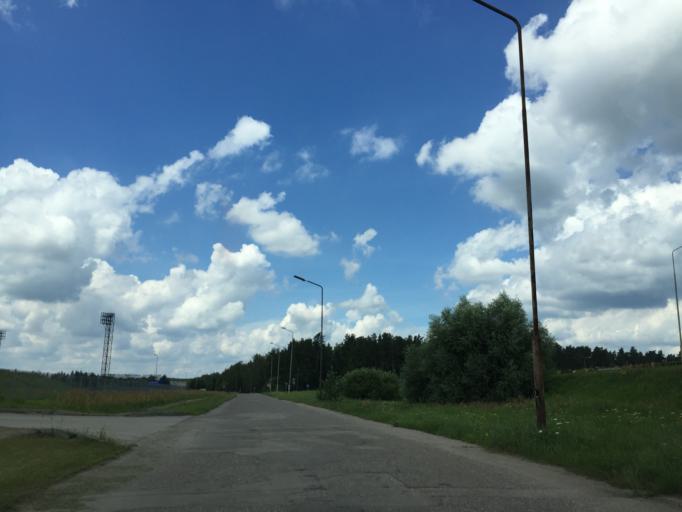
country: LV
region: Ozolnieku
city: Ozolnieki
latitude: 56.6654
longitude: 23.7743
